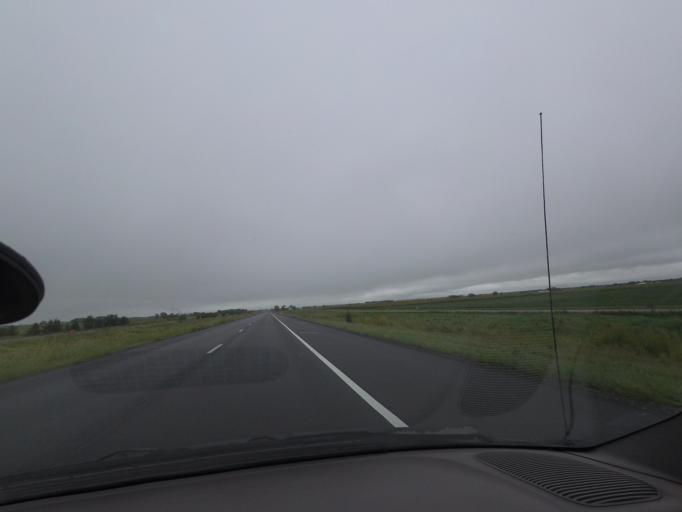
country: US
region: Illinois
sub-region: Macon County
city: Harristown
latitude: 39.8310
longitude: -89.1178
